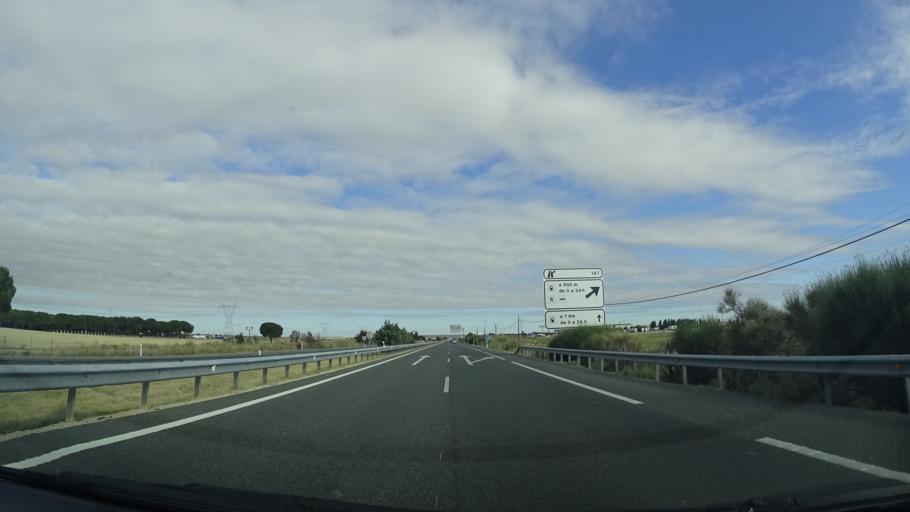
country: ES
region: Castille and Leon
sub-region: Provincia de Valladolid
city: San Vicente del Palacio
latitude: 41.2175
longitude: -4.8389
